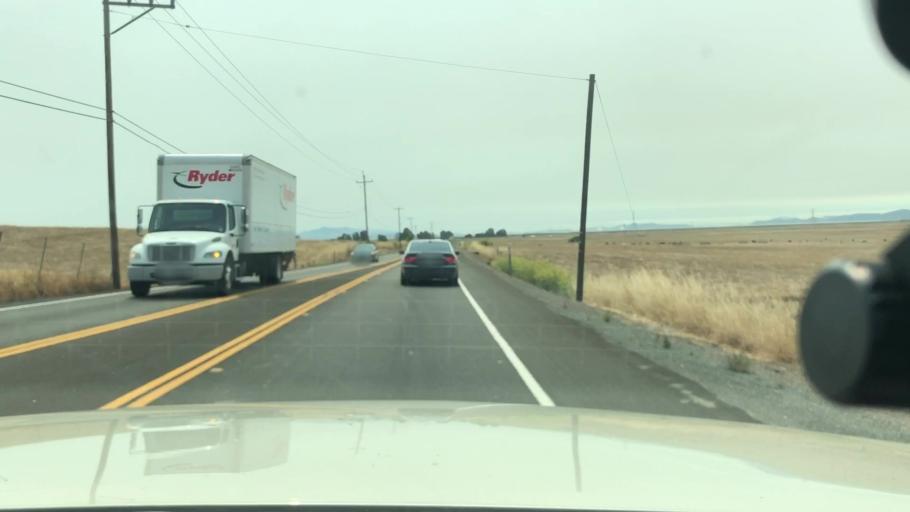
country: US
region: California
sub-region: Marin County
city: Black Point-Green Point
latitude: 38.1510
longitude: -122.4890
